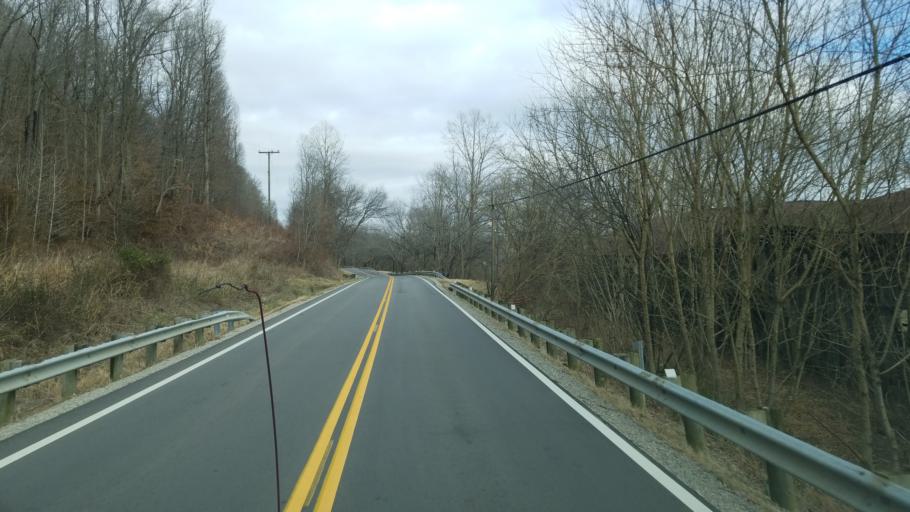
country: US
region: Kentucky
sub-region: Lewis County
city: Vanceburg
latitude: 38.6252
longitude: -83.1655
